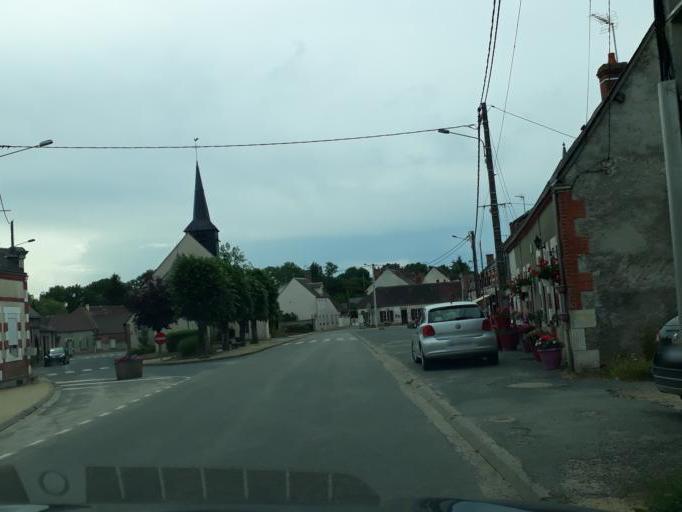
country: FR
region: Centre
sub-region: Departement du Loiret
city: Saint-Pere-sur-Loire
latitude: 47.7281
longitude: 2.3034
